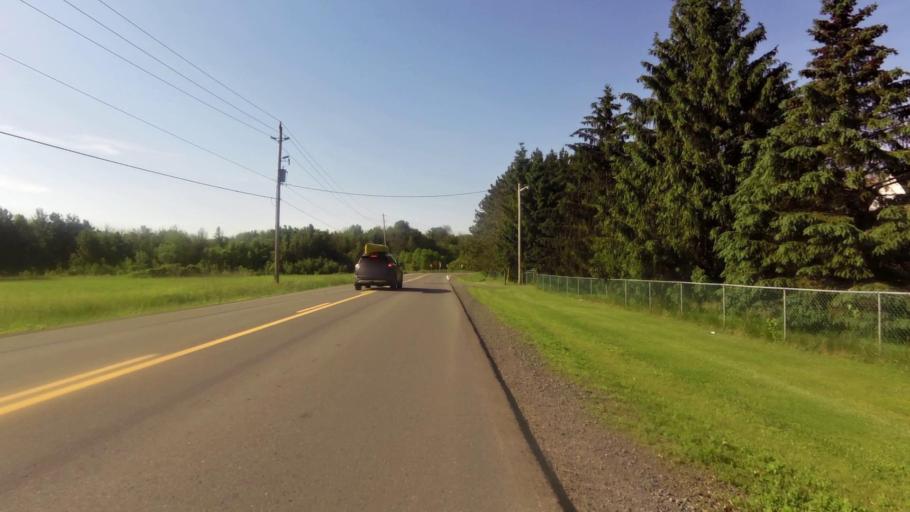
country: CA
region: Ontario
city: Ottawa
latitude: 45.2232
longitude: -75.5609
